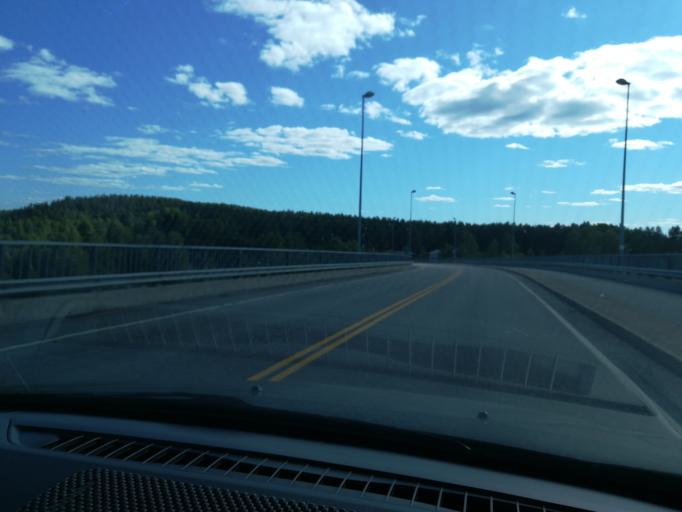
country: FI
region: Southern Savonia
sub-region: Mikkeli
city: Puumala
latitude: 61.5182
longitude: 28.1751
